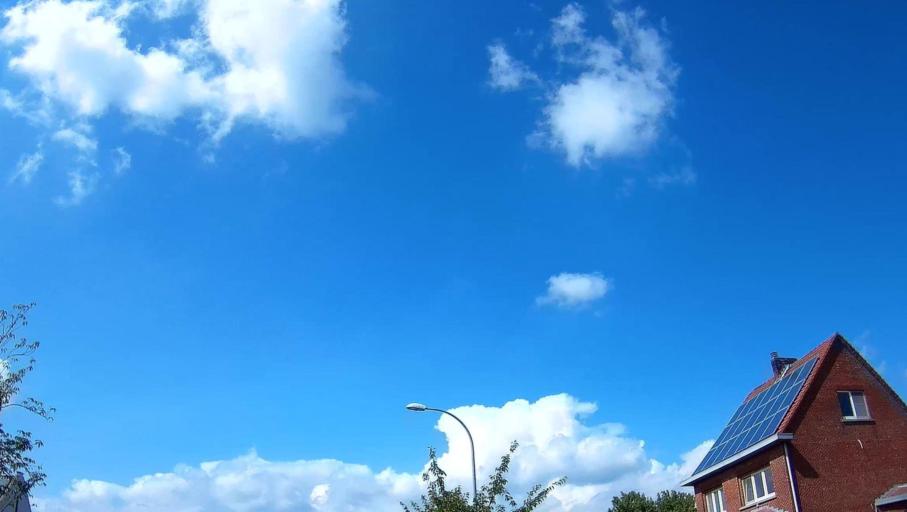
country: BE
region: Flanders
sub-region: Provincie Antwerpen
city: Balen
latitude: 51.1931
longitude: 5.2123
